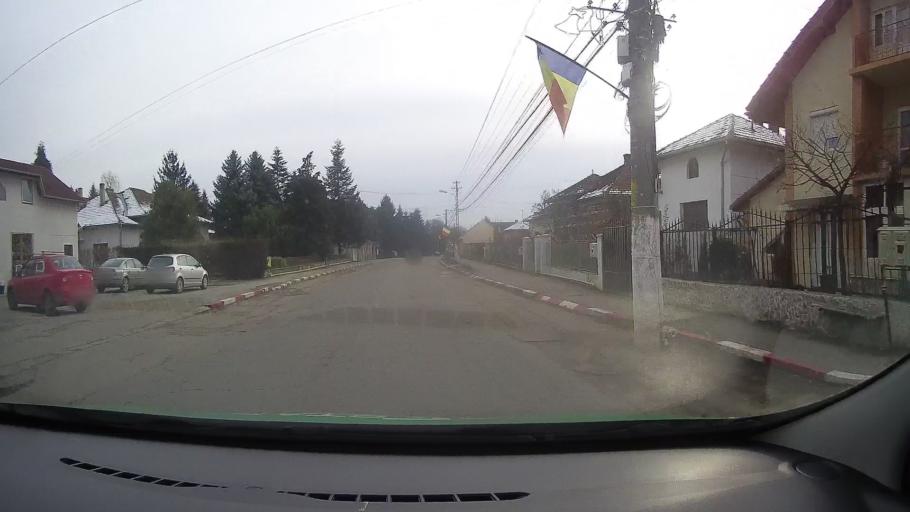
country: RO
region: Hunedoara
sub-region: Comuna Geoagiu
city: Geoagiu
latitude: 45.9214
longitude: 23.1995
